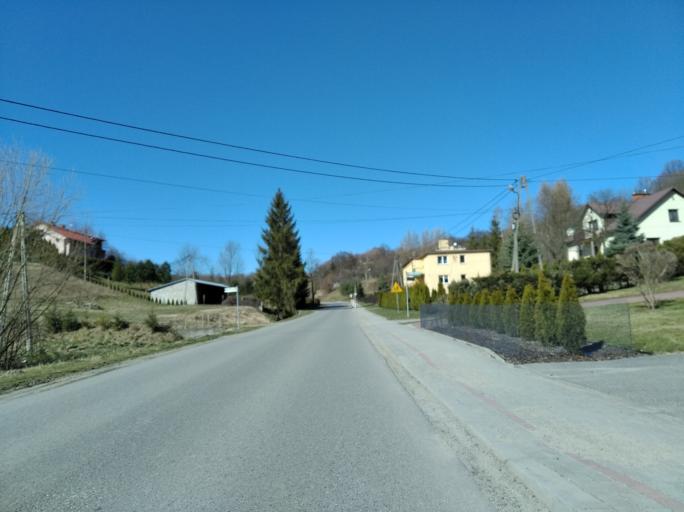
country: PL
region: Subcarpathian Voivodeship
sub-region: Powiat strzyzowski
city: Wisniowa
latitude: 49.8868
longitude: 21.6698
